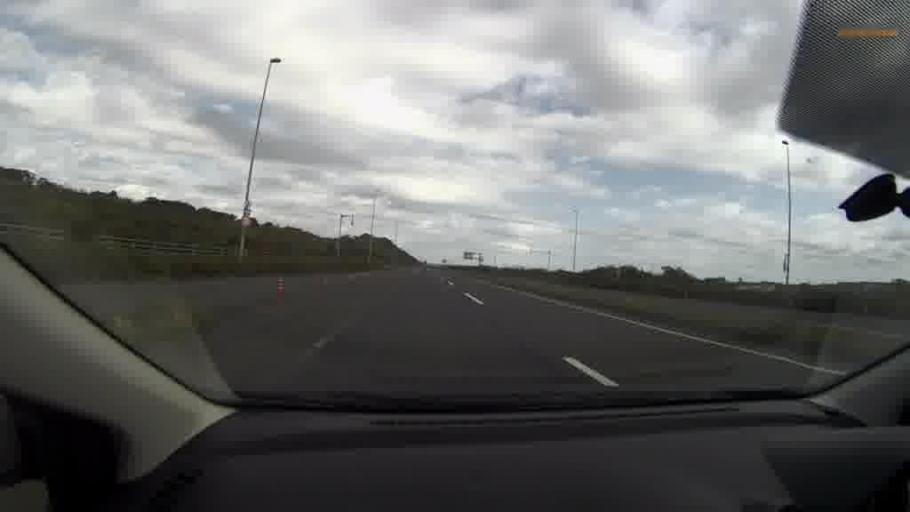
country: JP
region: Hokkaido
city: Kushiro
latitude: 43.0114
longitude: 144.2565
